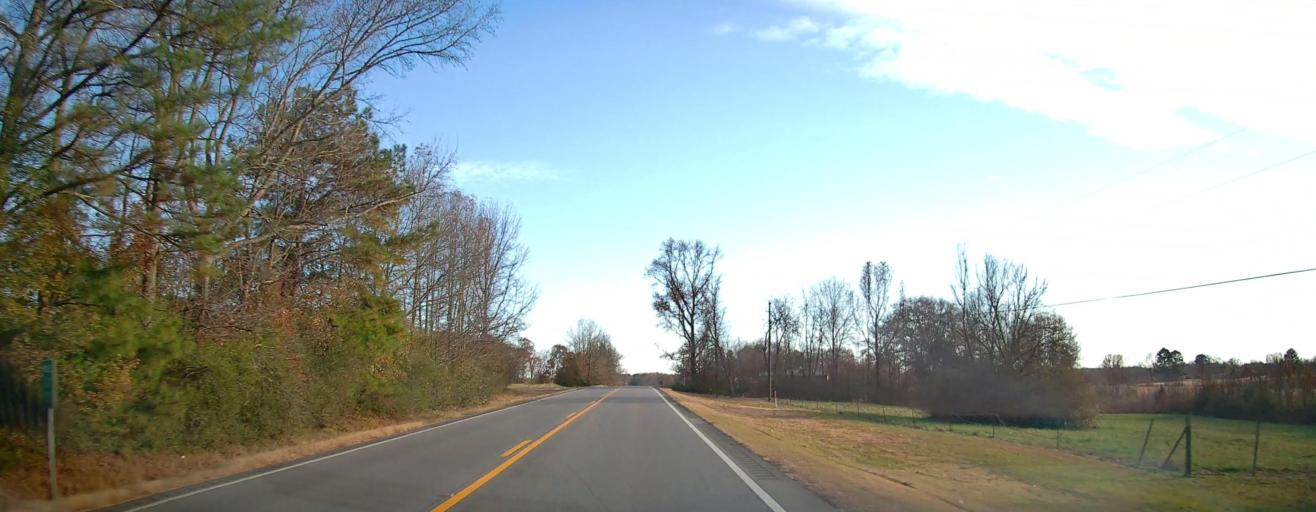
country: US
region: Alabama
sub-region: Marshall County
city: Arab
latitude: 34.3014
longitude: -86.5940
